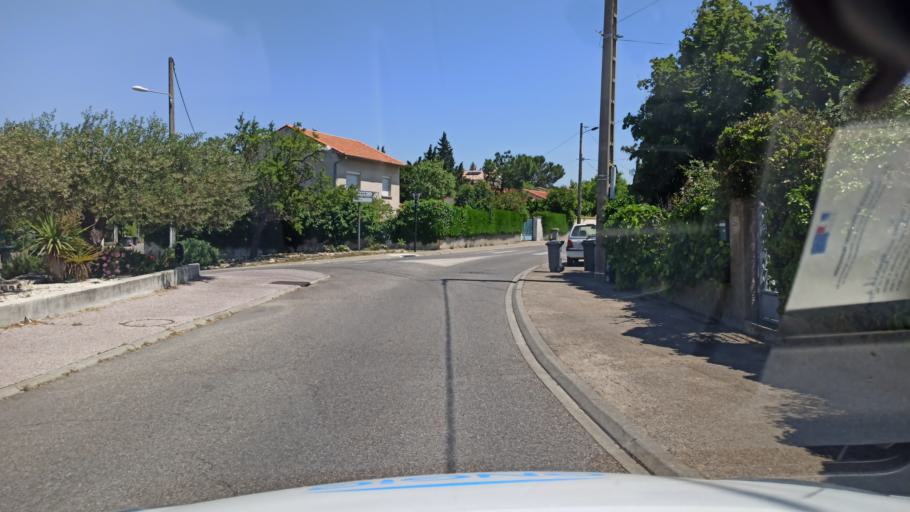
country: FR
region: Languedoc-Roussillon
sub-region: Departement du Gard
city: Les Angles
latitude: 43.9563
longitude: 4.7683
